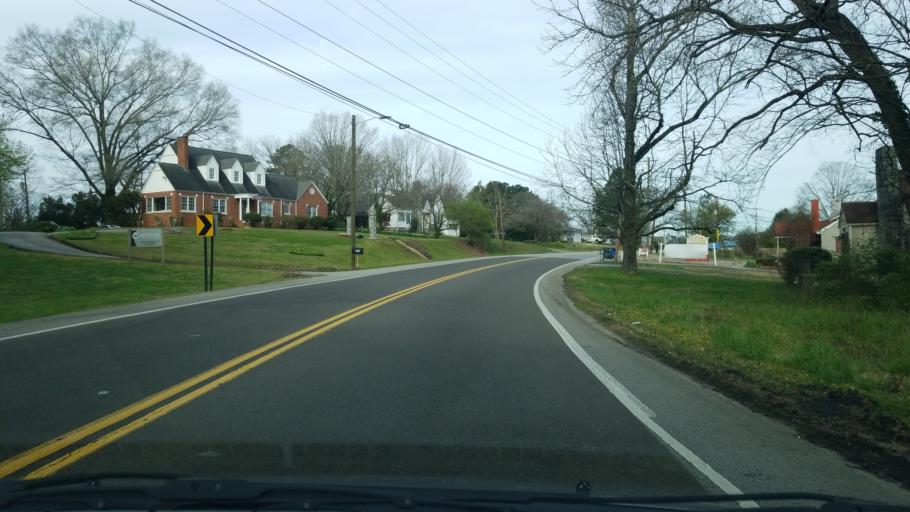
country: US
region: Tennessee
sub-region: Hamilton County
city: East Ridge
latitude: 35.0158
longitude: -85.2024
